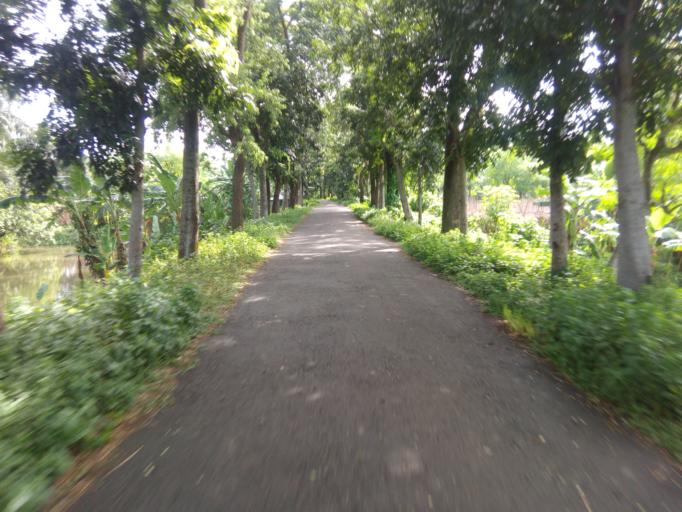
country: BD
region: Khulna
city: Kalia
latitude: 22.9524
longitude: 89.5492
